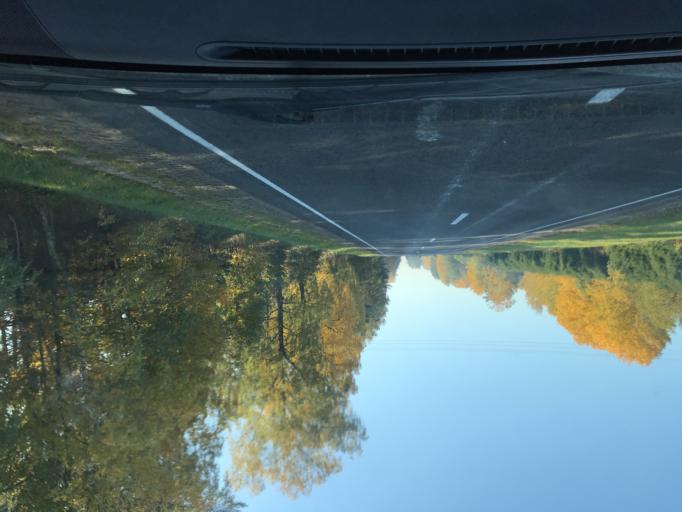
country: BY
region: Brest
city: Lyakhavichy
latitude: 52.9552
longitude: 26.2774
